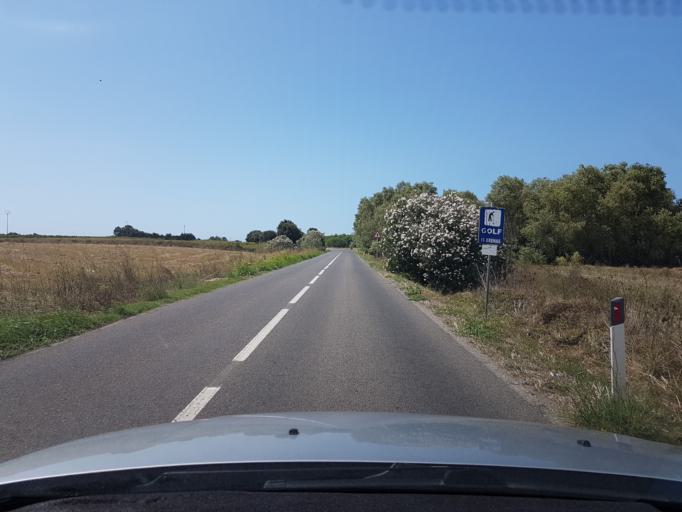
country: IT
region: Sardinia
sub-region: Provincia di Oristano
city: Riola Sardo
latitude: 40.0216
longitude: 8.4805
